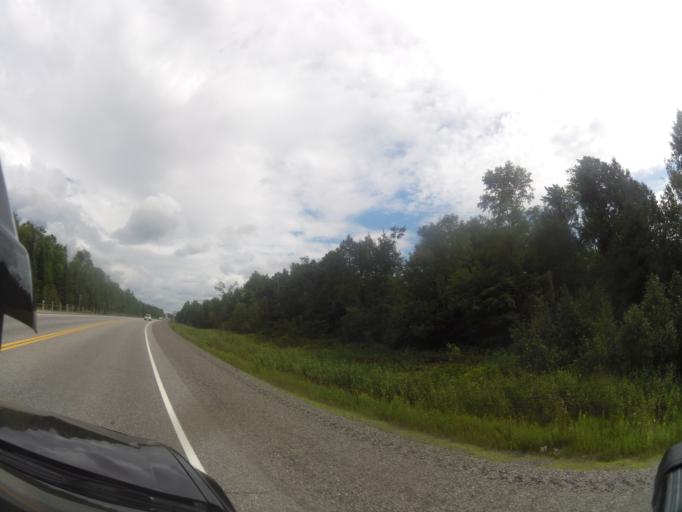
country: CA
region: Ontario
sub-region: Nipissing District
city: North Bay
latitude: 46.3707
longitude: -79.6996
